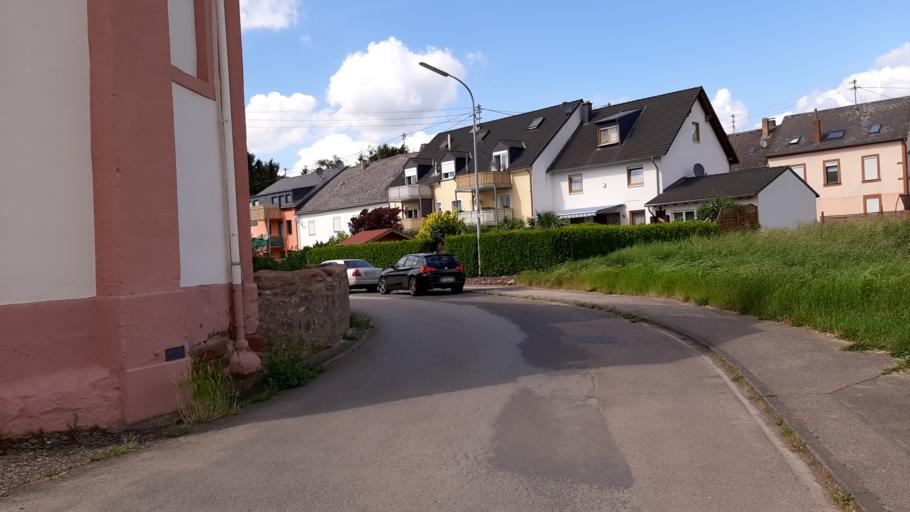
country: DE
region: Rheinland-Pfalz
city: Konz
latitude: 49.7132
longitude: 6.5869
